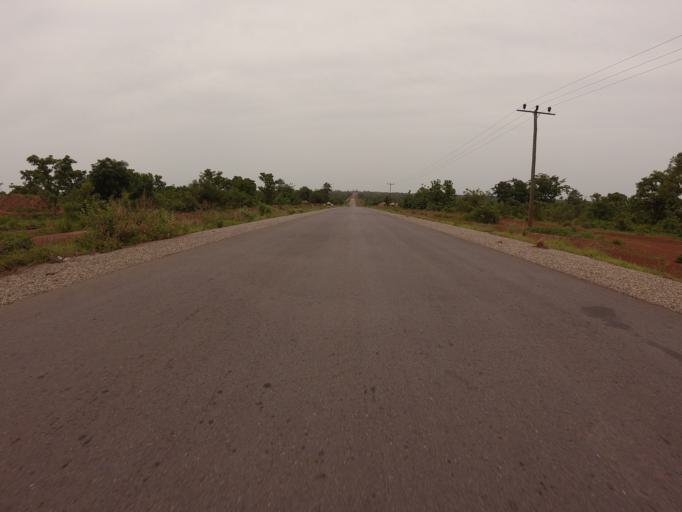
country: GH
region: Northern
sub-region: Yendi
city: Yendi
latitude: 9.2330
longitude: 0.0204
